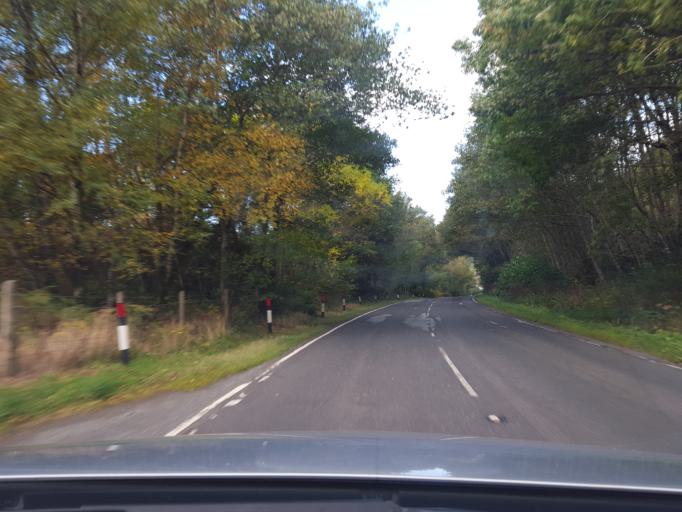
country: GB
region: Scotland
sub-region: Highland
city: Fort William
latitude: 57.2479
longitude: -5.4685
